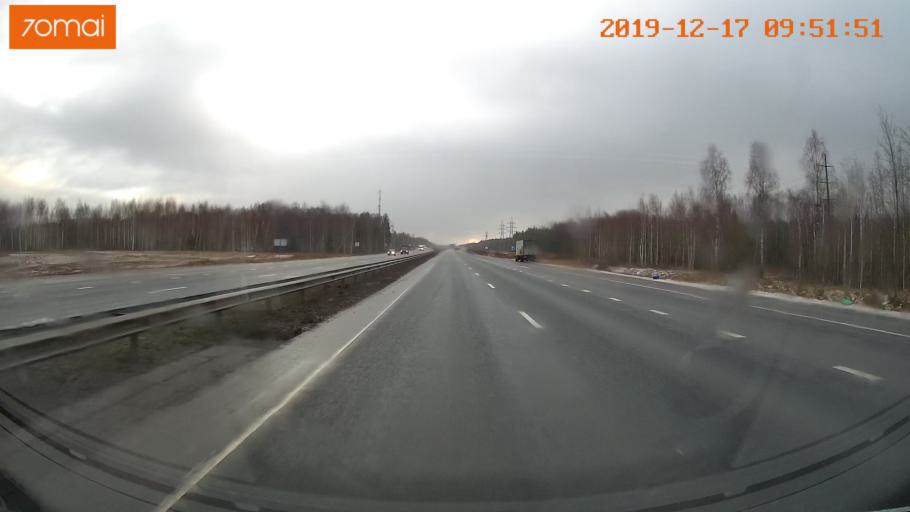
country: RU
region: Vladimir
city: Kommunar
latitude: 56.0394
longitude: 40.5274
